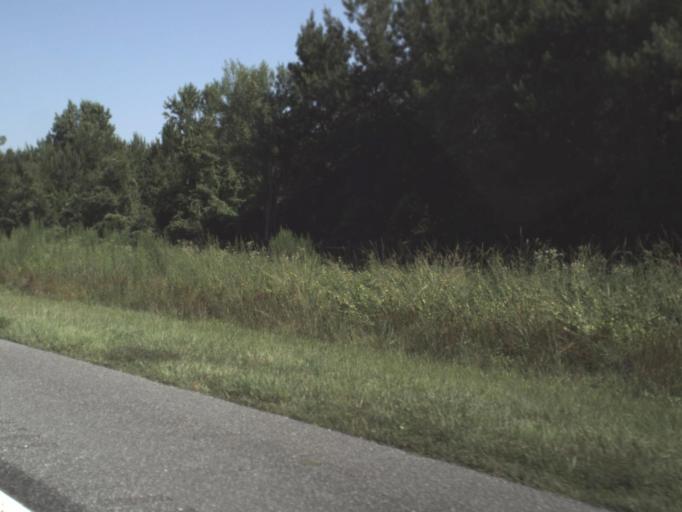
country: US
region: Florida
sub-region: Suwannee County
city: Live Oak
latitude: 30.3041
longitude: -82.9170
